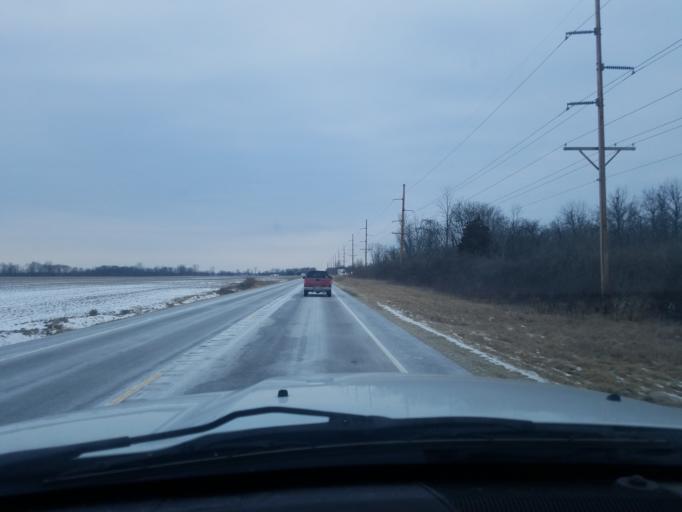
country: US
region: Indiana
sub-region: Randolph County
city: Farmland
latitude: 40.1712
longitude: -85.0978
